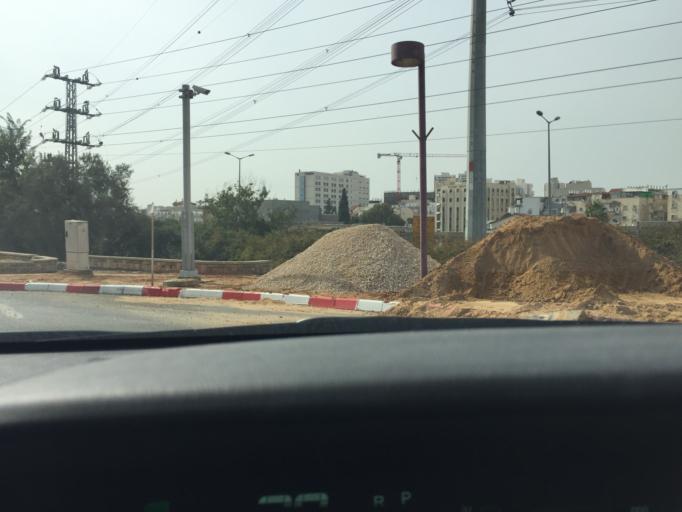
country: IL
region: Tel Aviv
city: Giv`at Shemu'el
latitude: 32.0721
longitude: 34.8436
